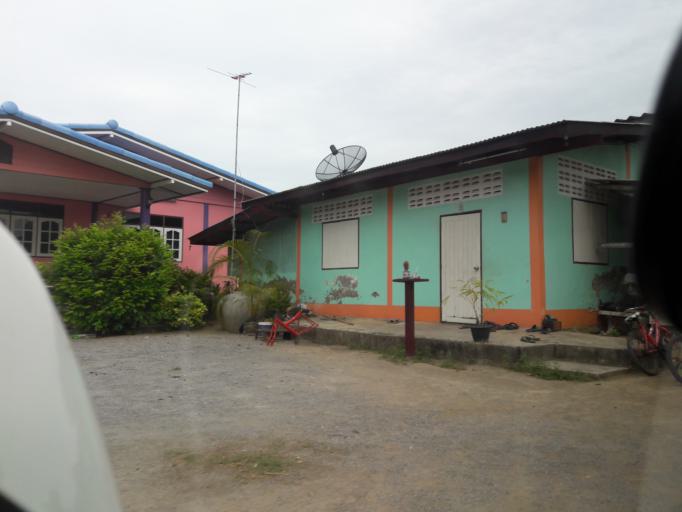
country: TH
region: Ratchaburi
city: Damnoen Saduak
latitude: 13.5814
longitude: 99.9593
